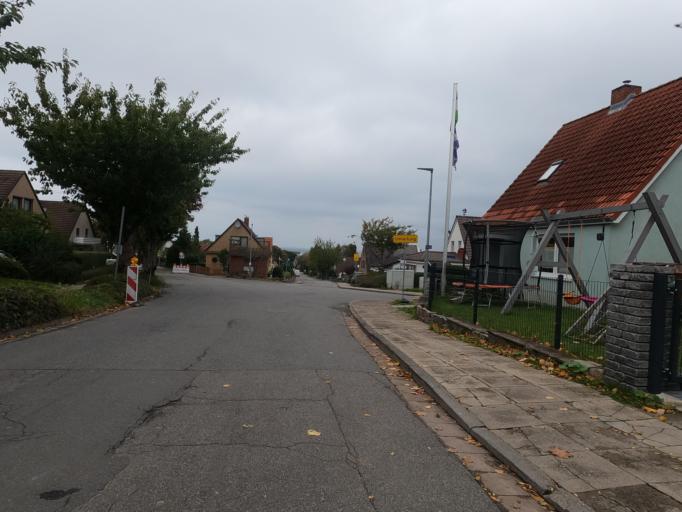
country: DE
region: Schleswig-Holstein
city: Heiligenhafen
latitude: 54.3660
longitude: 10.9843
